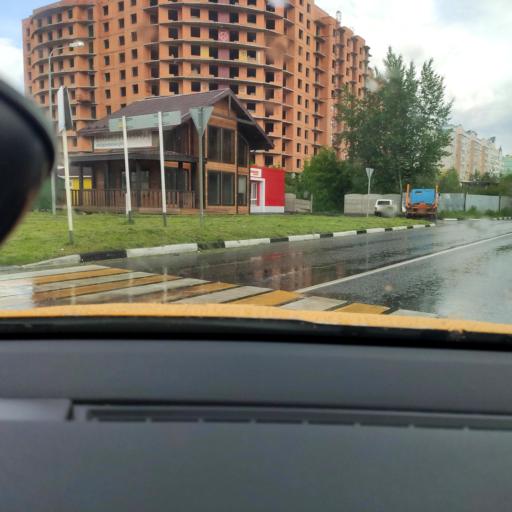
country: RU
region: Moskovskaya
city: Stupino
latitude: 54.8947
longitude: 38.0633
